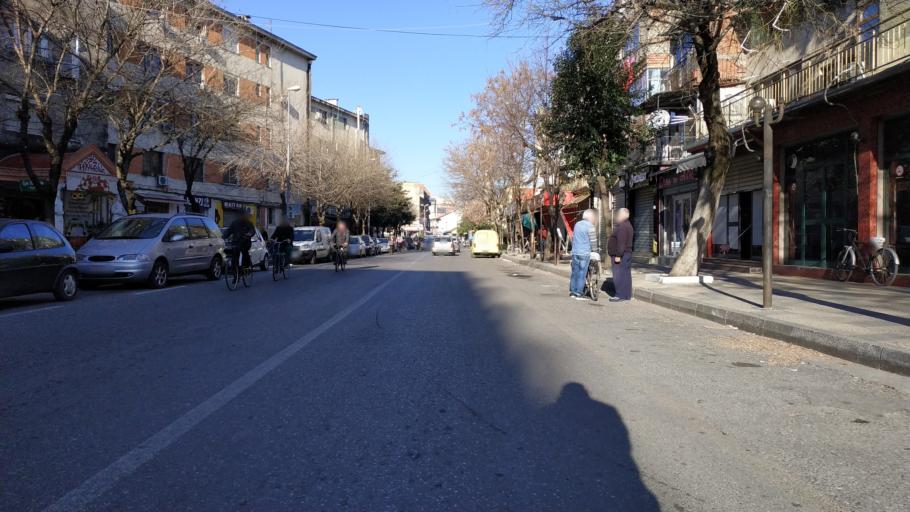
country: AL
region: Shkoder
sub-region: Rrethi i Shkodres
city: Shkoder
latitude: 42.0638
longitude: 19.5099
